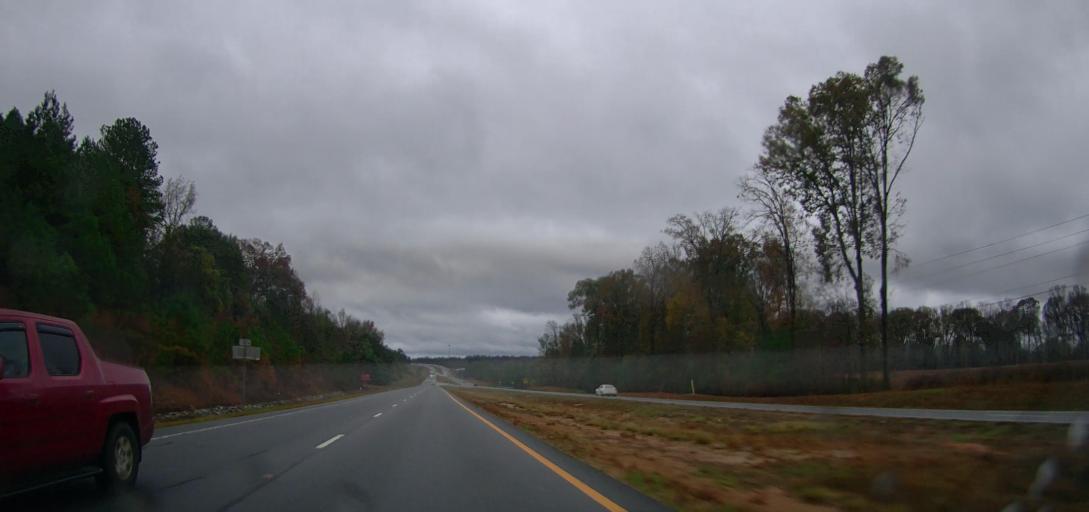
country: US
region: Georgia
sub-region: Jackson County
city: Commerce
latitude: 34.1675
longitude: -83.4454
